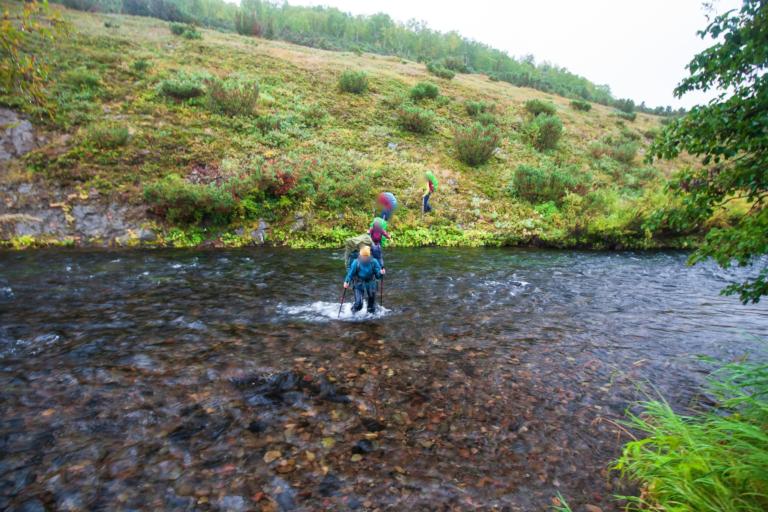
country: RU
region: Kamtsjatka
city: Yelizovo
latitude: 53.7383
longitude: 158.6916
